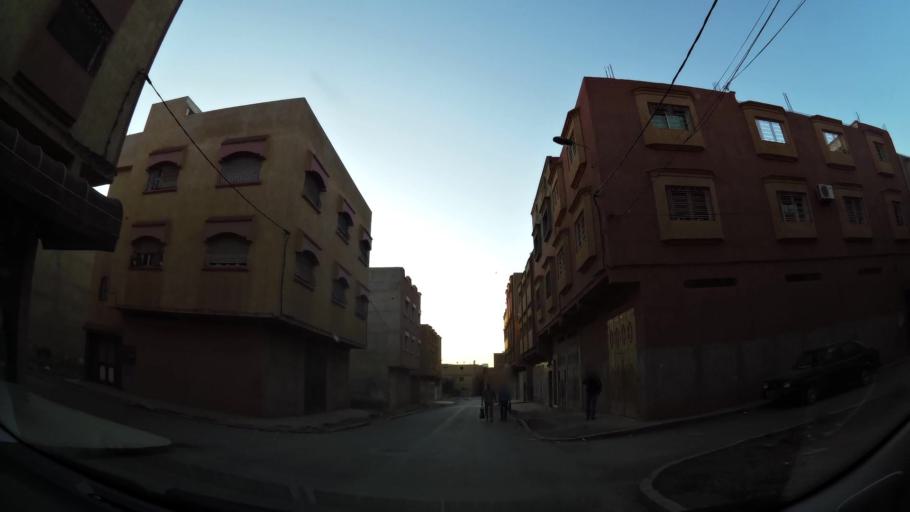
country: MA
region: Oriental
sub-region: Berkane-Taourirt
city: Berkane
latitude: 34.9199
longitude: -2.3136
